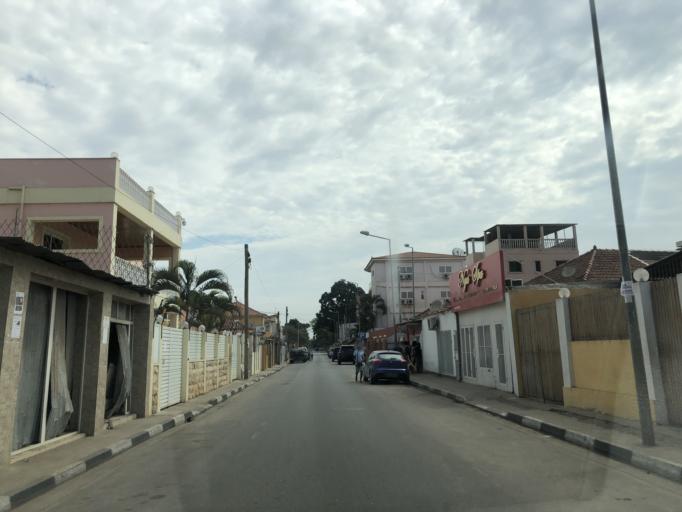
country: AO
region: Luanda
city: Luanda
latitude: -8.8219
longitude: 13.2497
